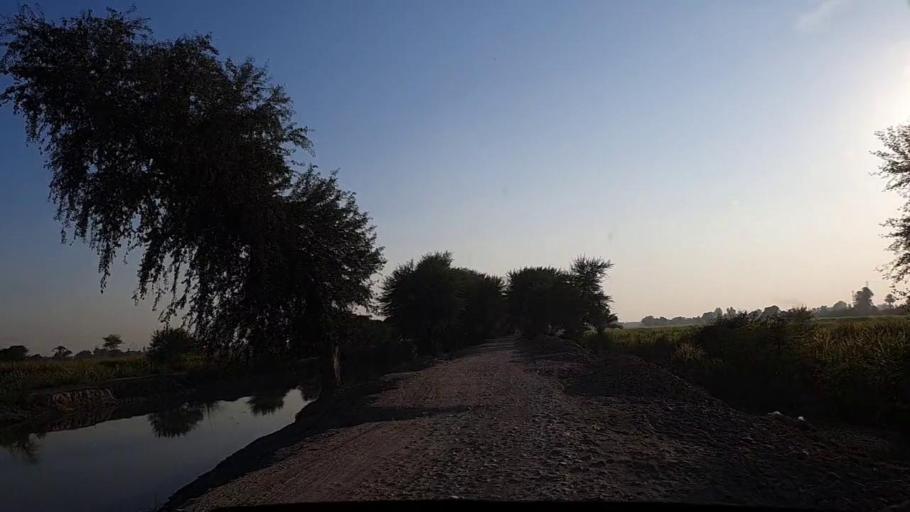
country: PK
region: Sindh
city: Sobhadero
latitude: 27.3995
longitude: 68.3887
